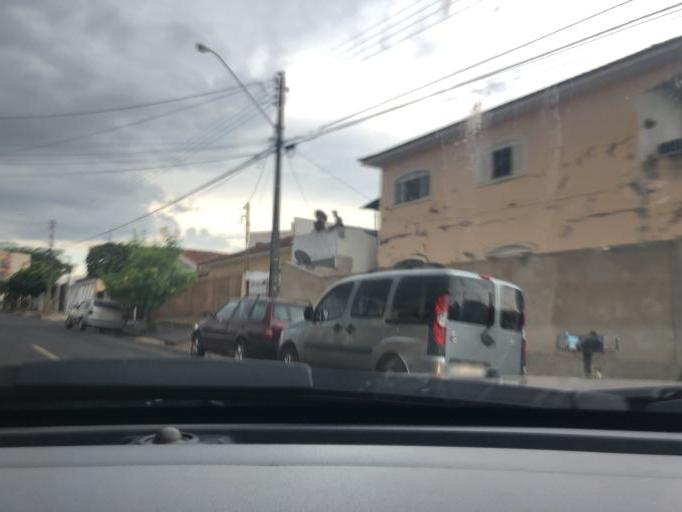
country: BR
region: Sao Paulo
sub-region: Sao Jose Do Rio Preto
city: Sao Jose do Rio Preto
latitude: -20.8422
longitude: -49.3828
